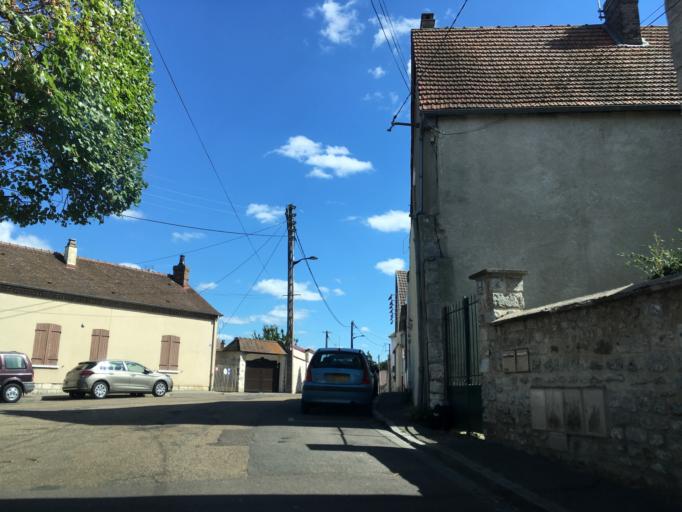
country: FR
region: Haute-Normandie
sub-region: Departement de l'Eure
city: Vernon
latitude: 49.0843
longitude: 1.4954
